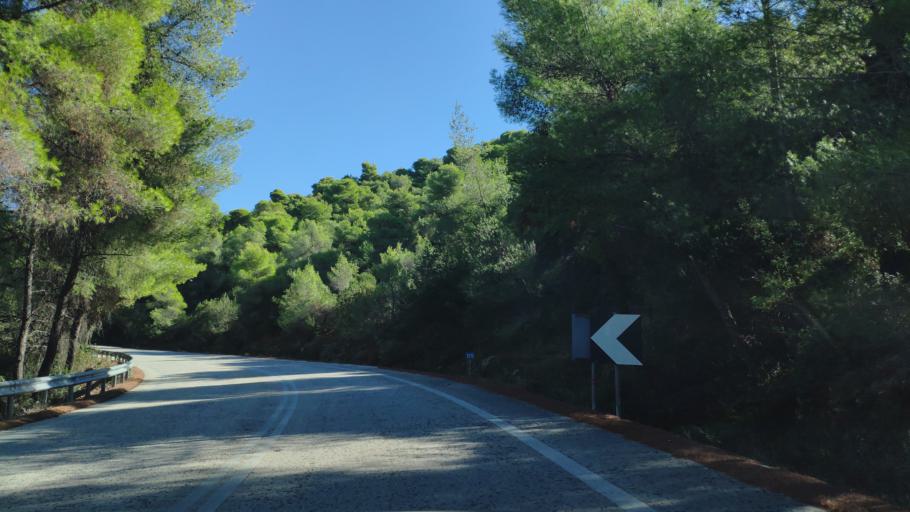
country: GR
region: Peloponnese
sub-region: Nomos Korinthias
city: Sofikon
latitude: 37.8274
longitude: 23.0441
